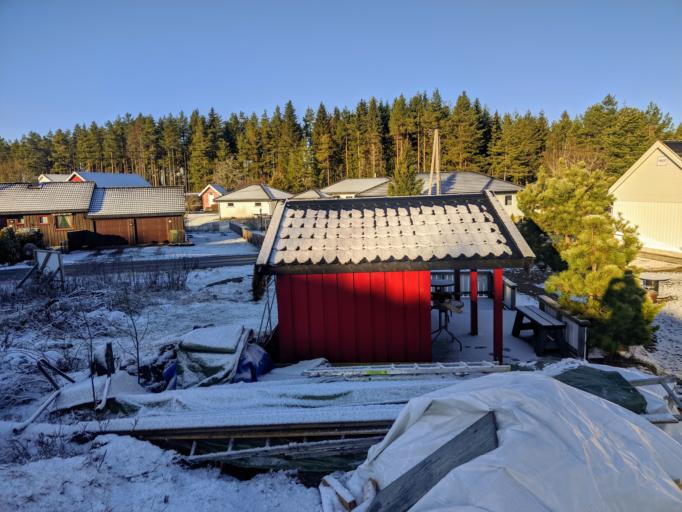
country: NO
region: Akershus
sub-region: Ullensaker
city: Jessheim
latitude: 60.1782
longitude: 11.2163
